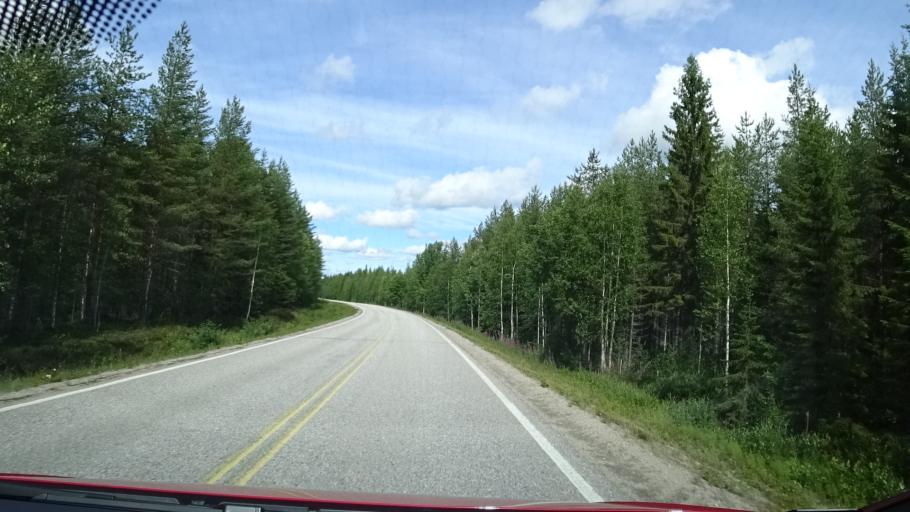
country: FI
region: Kainuu
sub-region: Kehys-Kainuu
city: Kuhmo
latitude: 64.4495
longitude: 29.7849
